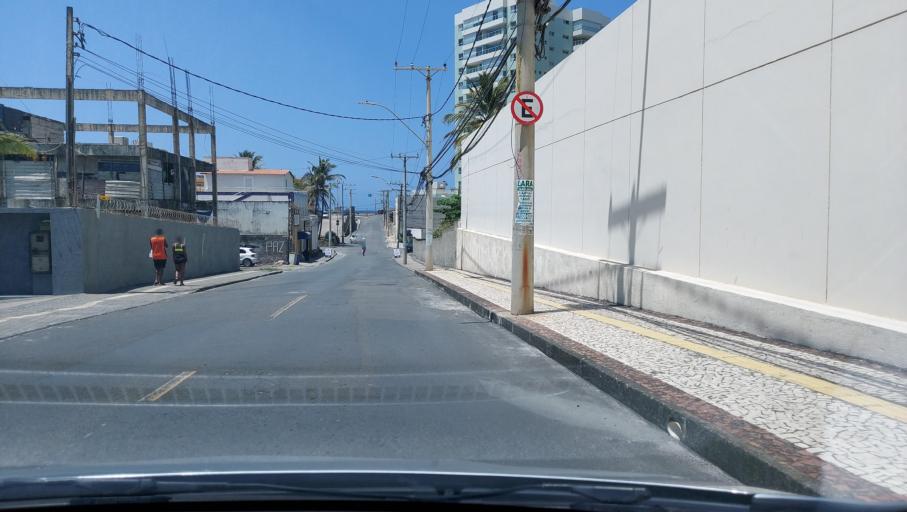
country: BR
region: Bahia
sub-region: Salvador
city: Salvador
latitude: -12.9879
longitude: -38.4378
